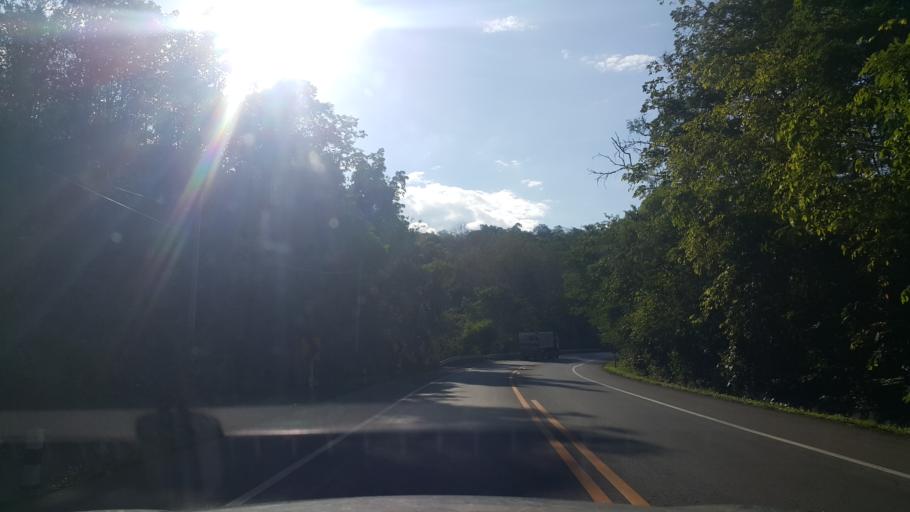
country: TH
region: Phayao
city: Phayao
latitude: 19.0849
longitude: 99.8175
